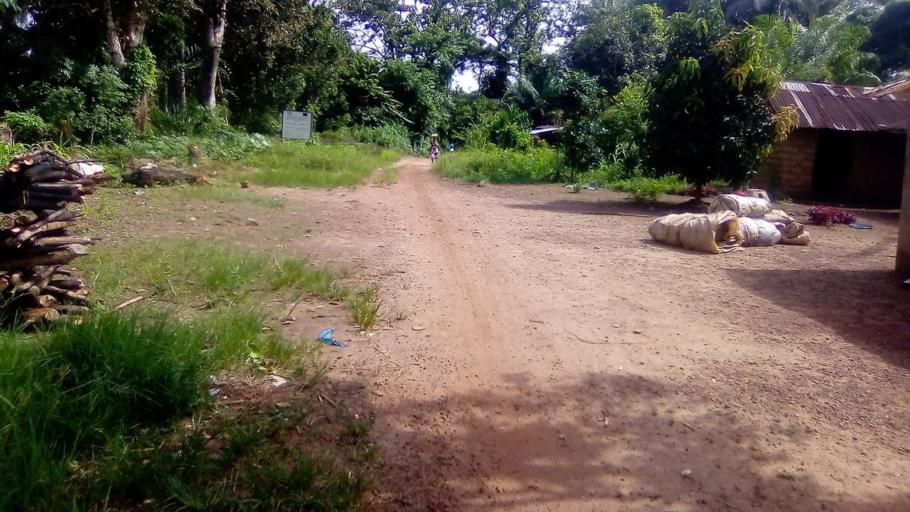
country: SL
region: Southern Province
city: Pujehun
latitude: 7.3745
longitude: -11.7285
